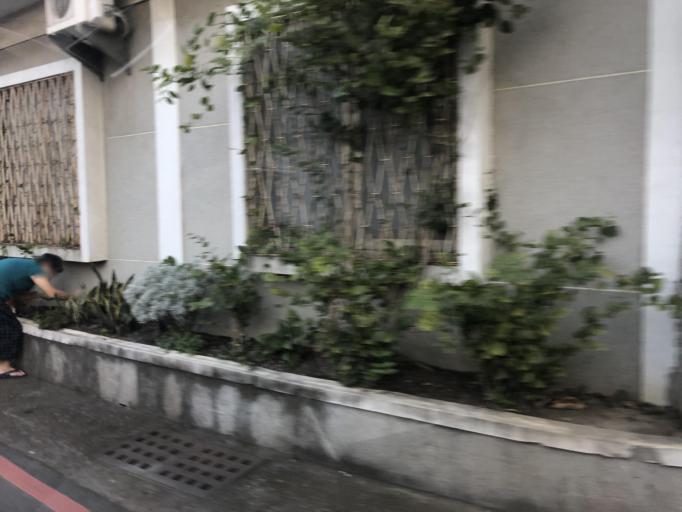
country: TW
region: Taiwan
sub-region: Tainan
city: Tainan
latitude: 23.1305
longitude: 120.2508
